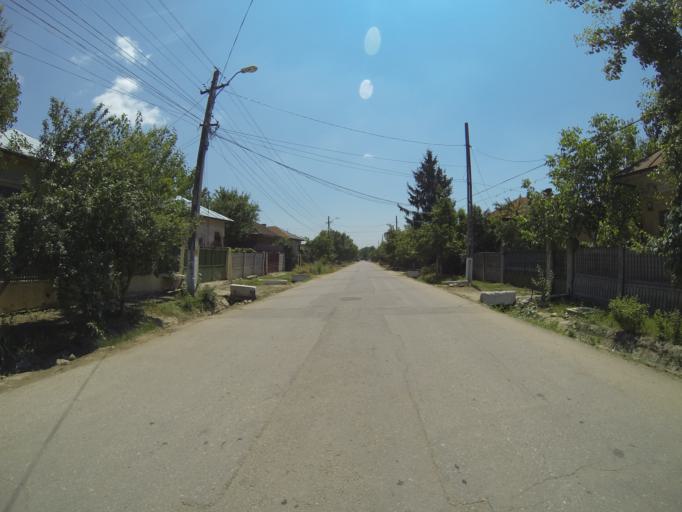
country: RO
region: Dolj
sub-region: Comuna Segarcea
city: Segarcea
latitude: 44.0921
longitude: 23.7463
